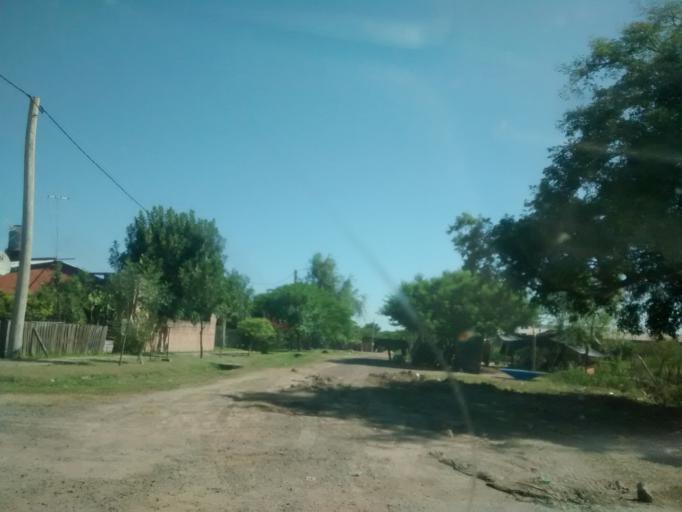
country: AR
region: Chaco
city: Fontana
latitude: -27.4000
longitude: -58.9901
